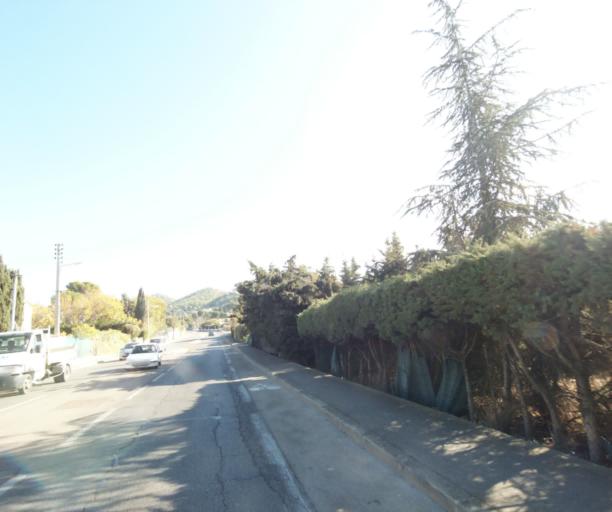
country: FR
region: Provence-Alpes-Cote d'Azur
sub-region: Departement des Bouches-du-Rhone
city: Allauch
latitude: 43.3383
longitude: 5.4754
